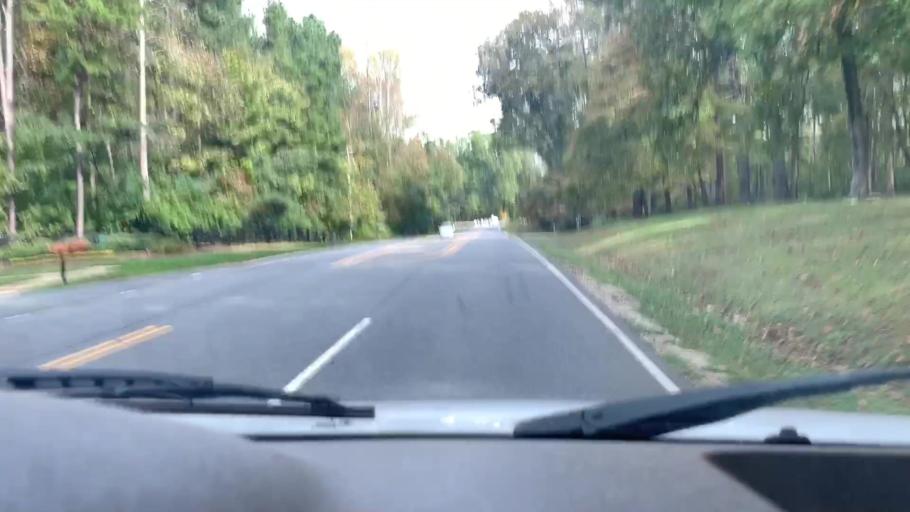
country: US
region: North Carolina
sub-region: Mecklenburg County
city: Huntersville
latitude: 35.4240
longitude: -80.7940
